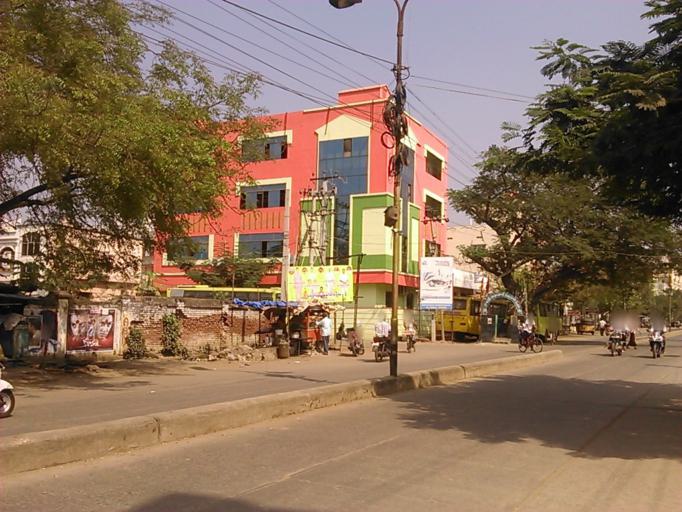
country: IN
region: Andhra Pradesh
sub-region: Guntur
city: Bhattiprolu
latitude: 16.2384
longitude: 80.6547
